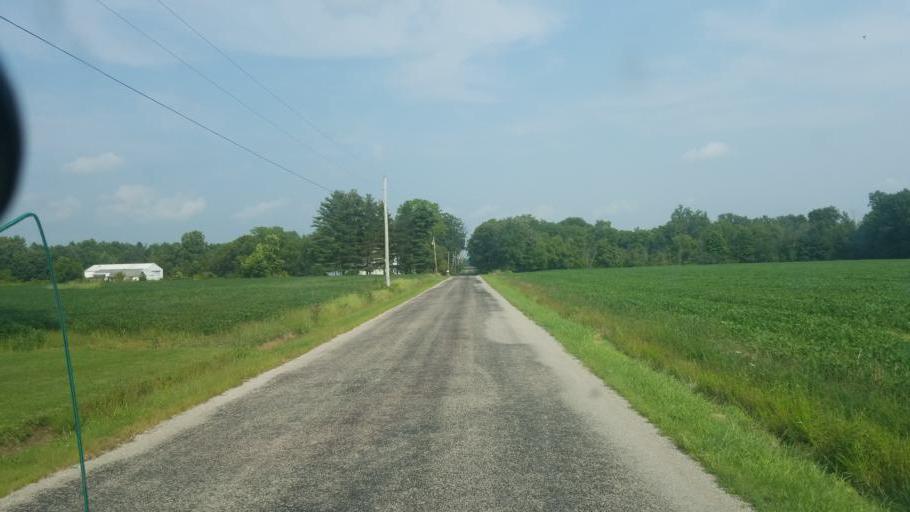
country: US
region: Ohio
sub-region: Lorain County
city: Wellington
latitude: 41.1294
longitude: -82.1293
